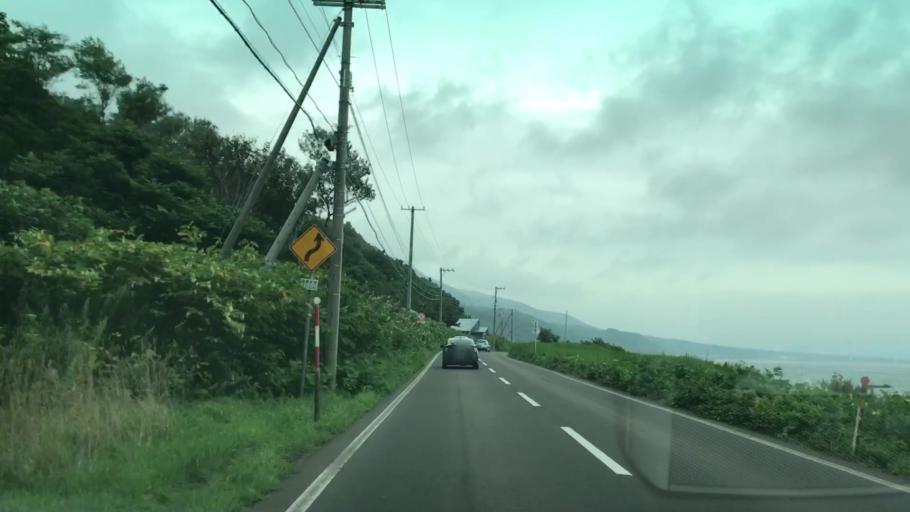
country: JP
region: Hokkaido
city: Iwanai
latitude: 42.8037
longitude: 140.3067
